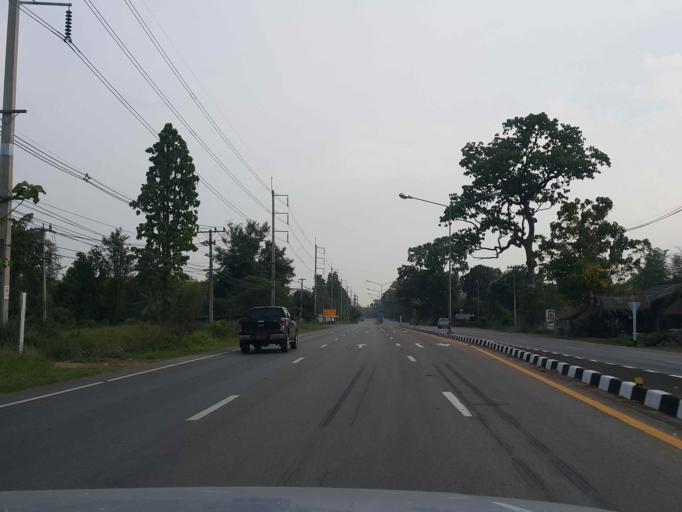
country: TH
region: Chiang Mai
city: Mae Taeng
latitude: 19.1717
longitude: 98.9491
